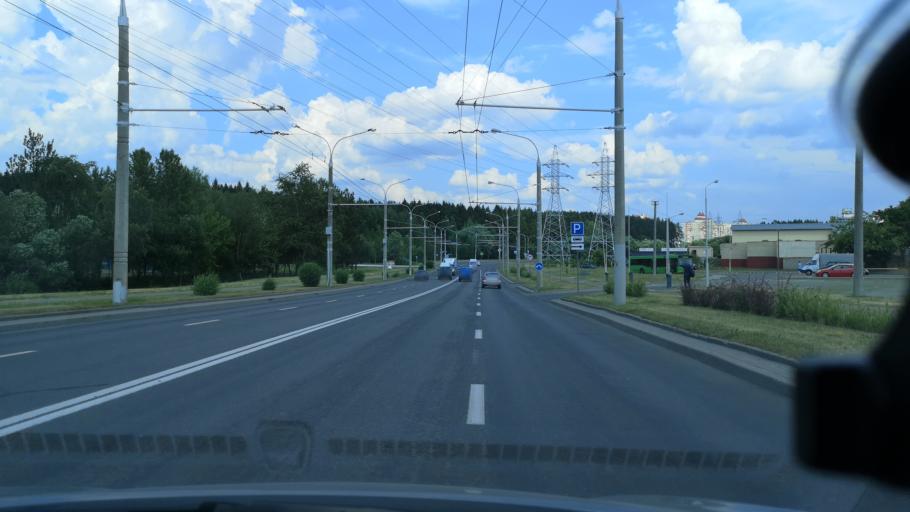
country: BY
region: Minsk
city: Borovlyany
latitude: 53.9430
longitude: 27.6536
